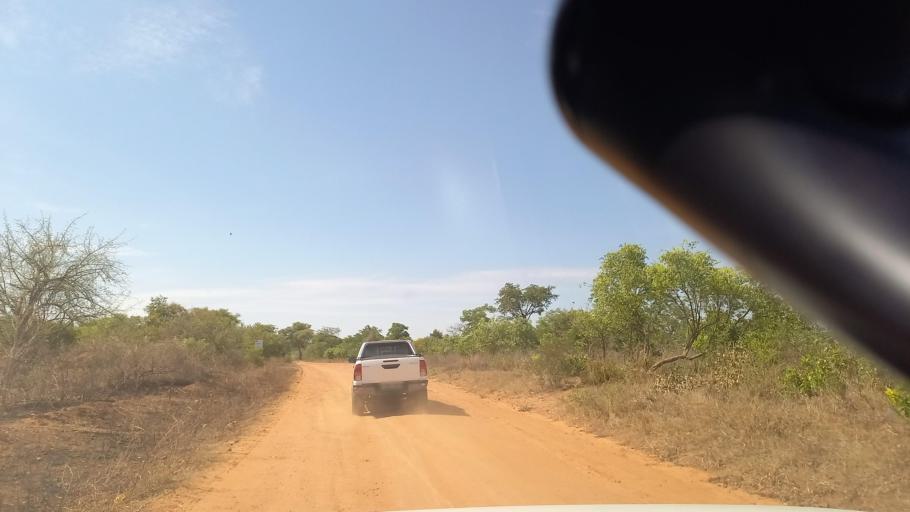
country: ZM
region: Southern
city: Mazabuka
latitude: -16.0353
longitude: 27.6176
